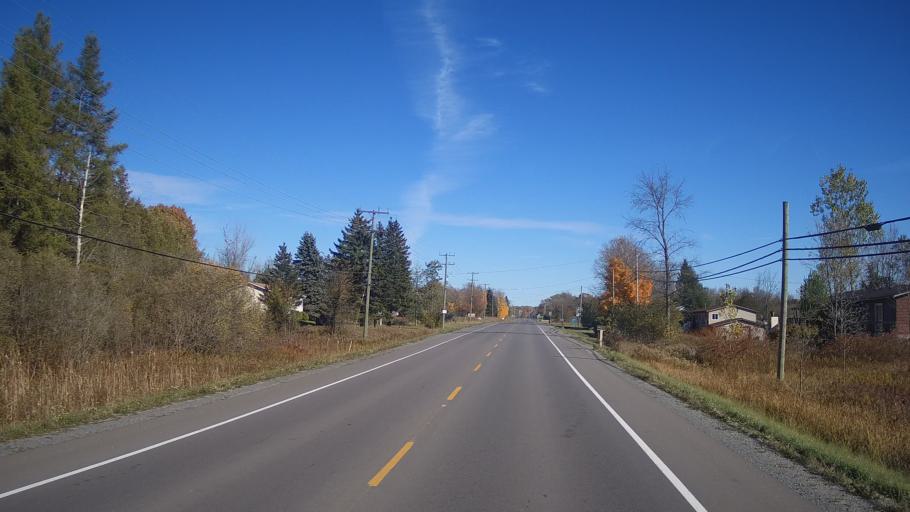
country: CA
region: Ontario
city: Kingston
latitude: 44.4060
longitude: -76.6251
